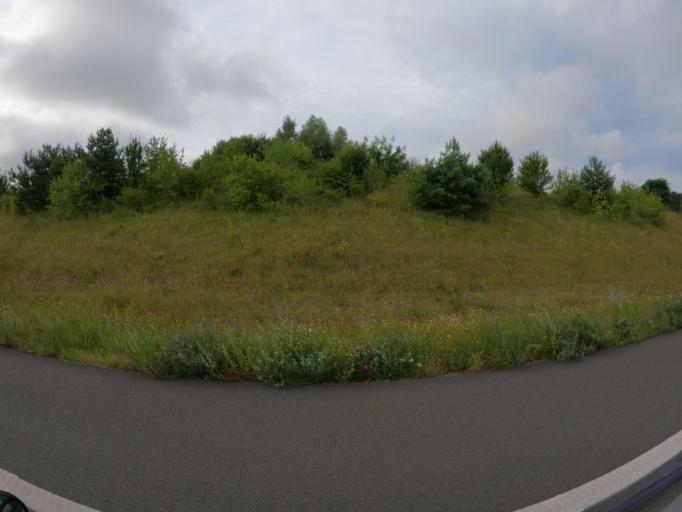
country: FR
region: Centre
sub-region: Departement d'Indre-et-Loire
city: Monts
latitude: 47.3067
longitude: 0.6295
